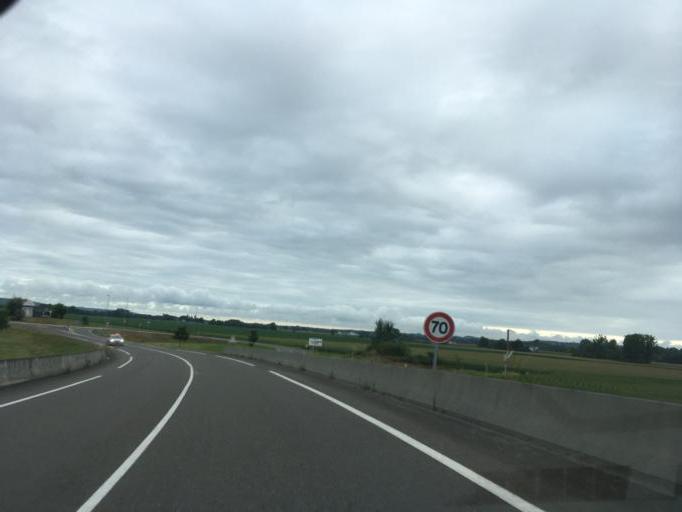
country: FR
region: Midi-Pyrenees
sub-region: Departement des Hautes-Pyrenees
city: Maubourguet
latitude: 43.4838
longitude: 0.0177
